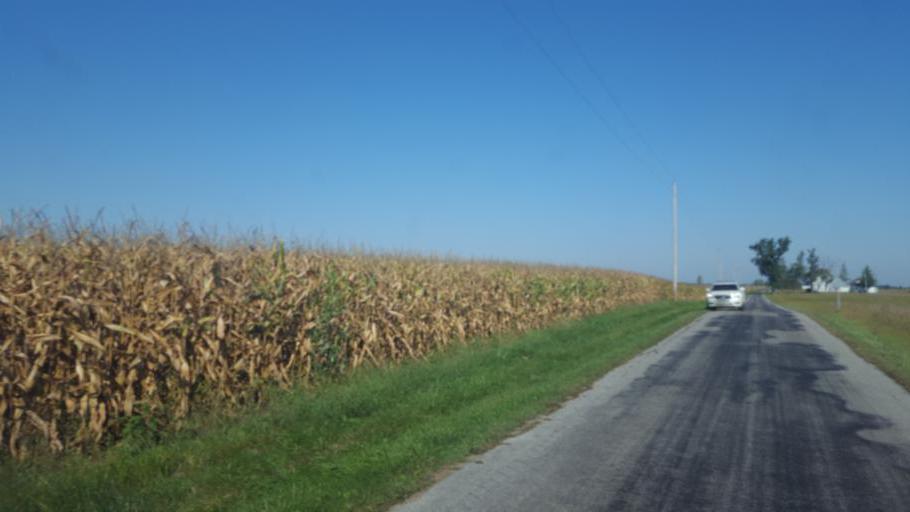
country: US
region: Ohio
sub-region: Union County
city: Richwood
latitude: 40.5143
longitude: -83.4523
